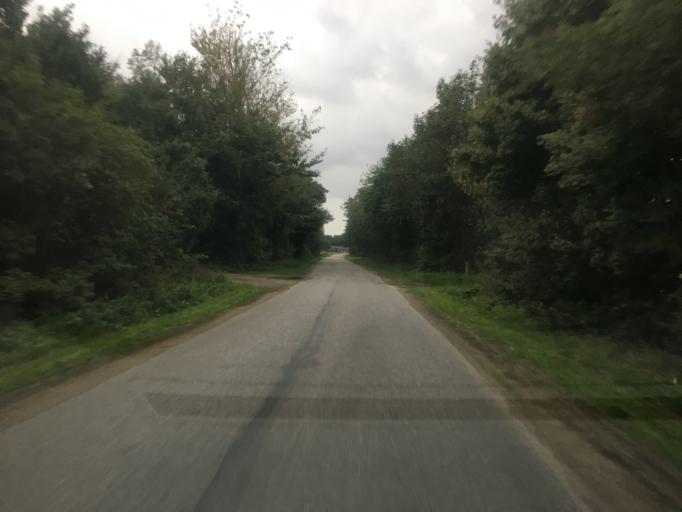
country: DK
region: South Denmark
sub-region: Tonder Kommune
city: Logumkloster
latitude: 55.0017
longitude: 9.0179
